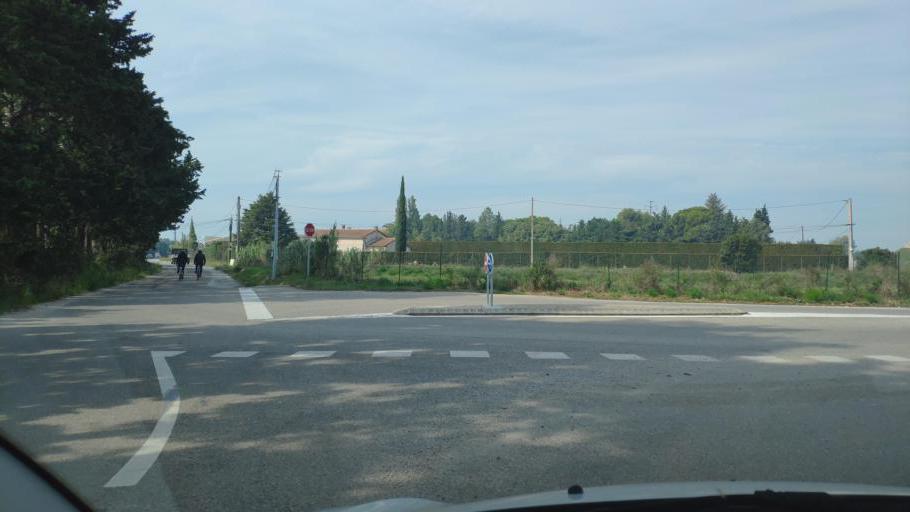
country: FR
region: Provence-Alpes-Cote d'Azur
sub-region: Departement du Vaucluse
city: Carpentras
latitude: 44.0342
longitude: 5.0330
